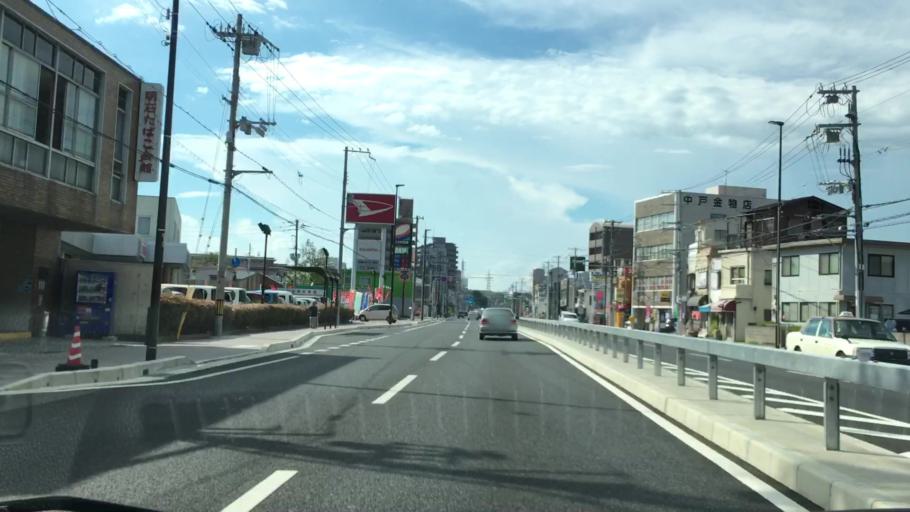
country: JP
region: Hyogo
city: Akashi
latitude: 34.6505
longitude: 134.9808
